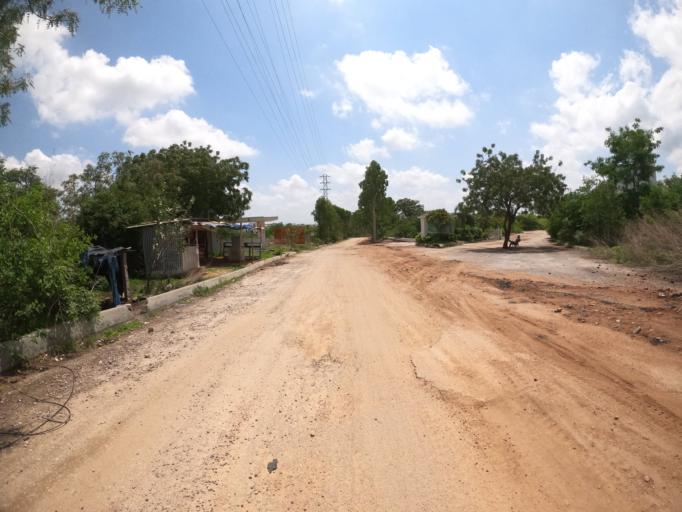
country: IN
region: Telangana
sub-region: Medak
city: Serilingampalle
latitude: 17.3769
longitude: 78.3211
